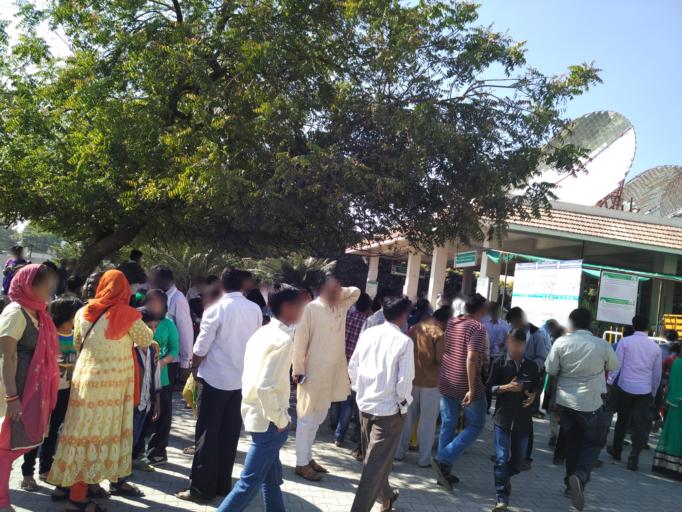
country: IN
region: Maharashtra
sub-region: Ahmadnagar
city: Shirdi
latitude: 19.7700
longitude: 74.4716
